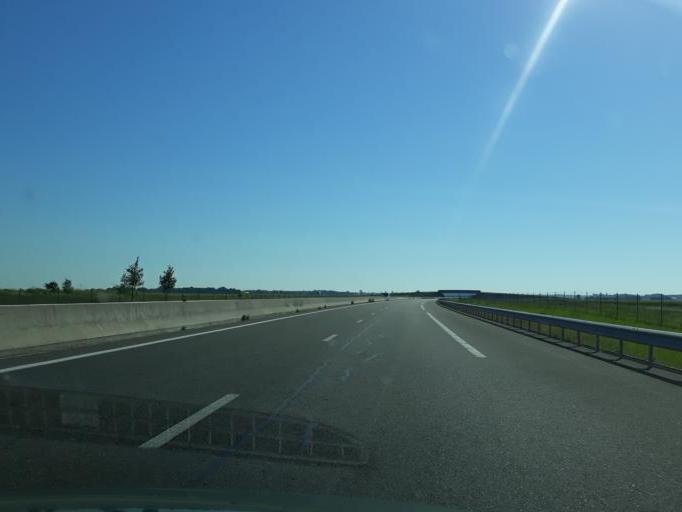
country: FR
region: Centre
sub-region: Departement du Loiret
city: Corbeilles
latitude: 48.0876
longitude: 2.4998
